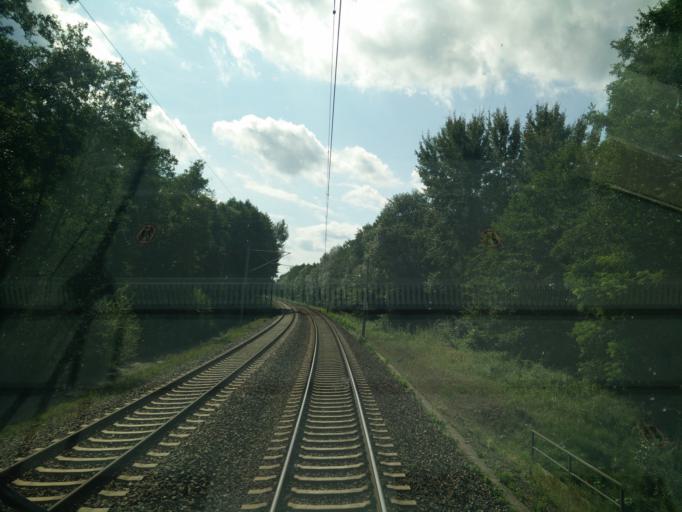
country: DE
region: Brandenburg
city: Bestensee
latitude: 52.2110
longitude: 13.6183
